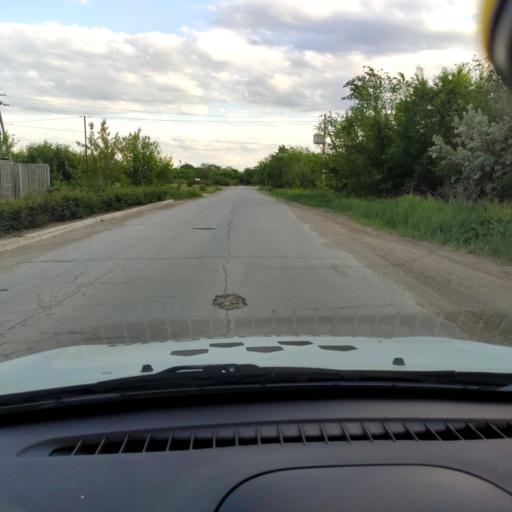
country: RU
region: Samara
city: Podstepki
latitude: 53.5791
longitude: 49.2285
